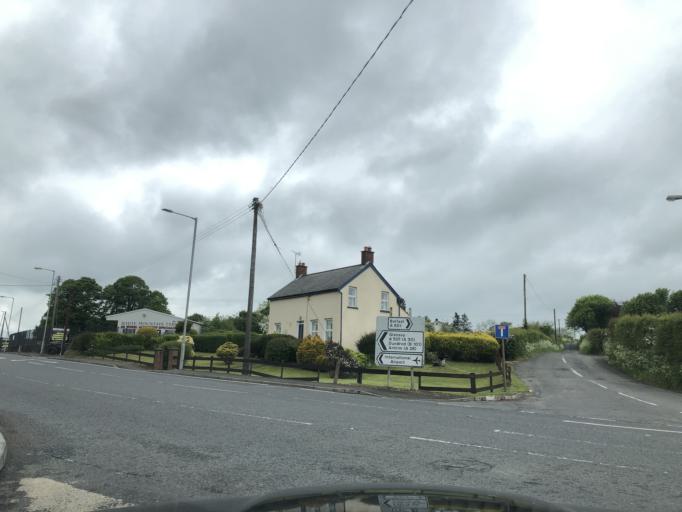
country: GB
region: Northern Ireland
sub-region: Lisburn District
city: Lisburn
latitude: 54.5486
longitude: -6.0764
